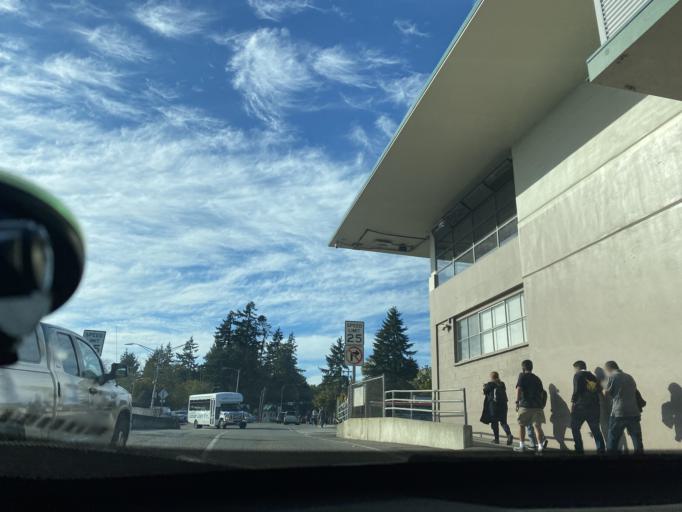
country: US
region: Washington
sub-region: Kitsap County
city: Bainbridge Island
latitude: 47.6230
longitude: -122.5110
